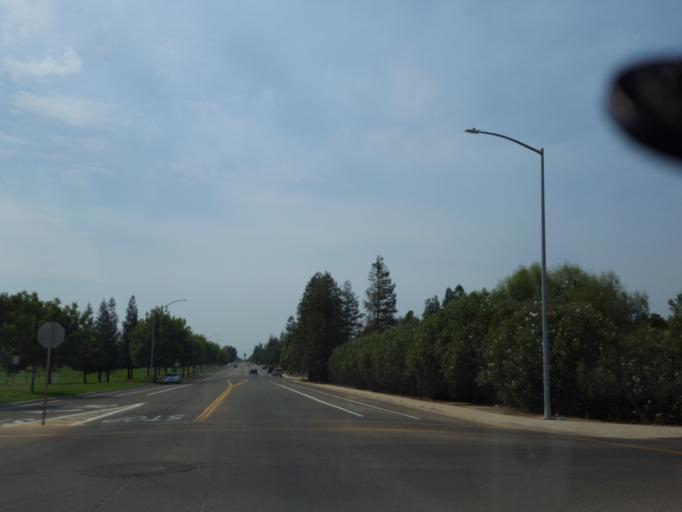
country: US
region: California
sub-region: Fresno County
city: Reedley
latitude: 36.6115
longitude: -119.4430
